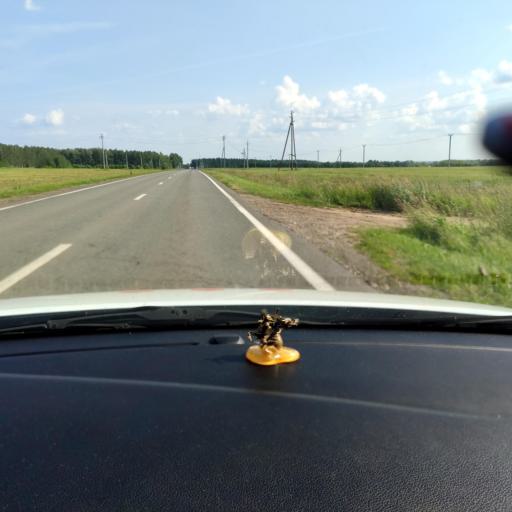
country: RU
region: Tatarstan
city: Stolbishchi
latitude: 55.4451
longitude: 49.3125
